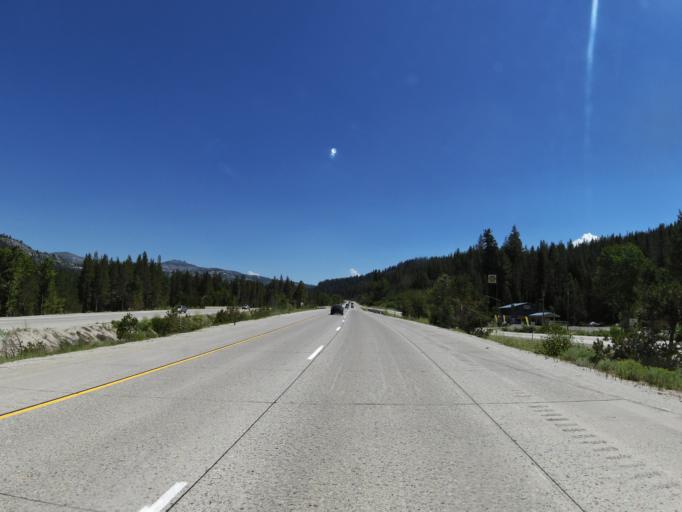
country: US
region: California
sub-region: Nevada County
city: Truckee
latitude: 39.3137
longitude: -120.4472
